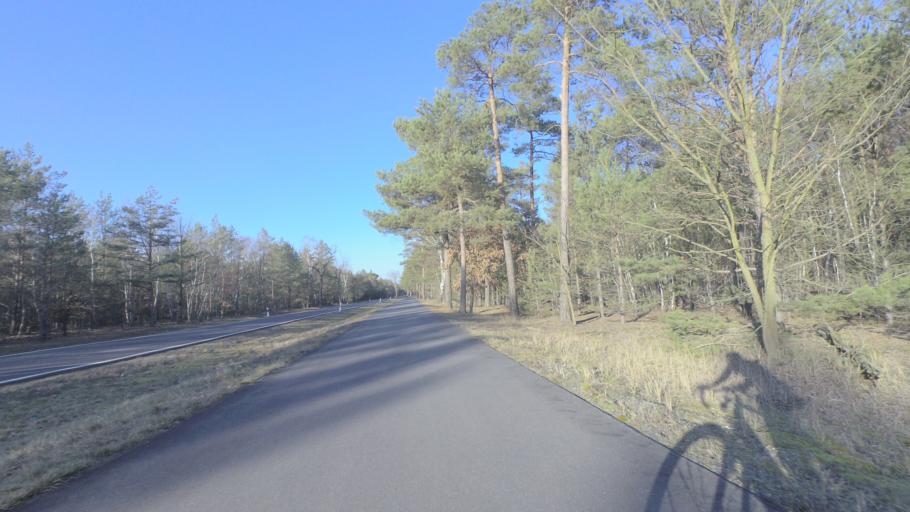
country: DE
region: Brandenburg
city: Sperenberg
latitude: 52.0257
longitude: 13.3185
